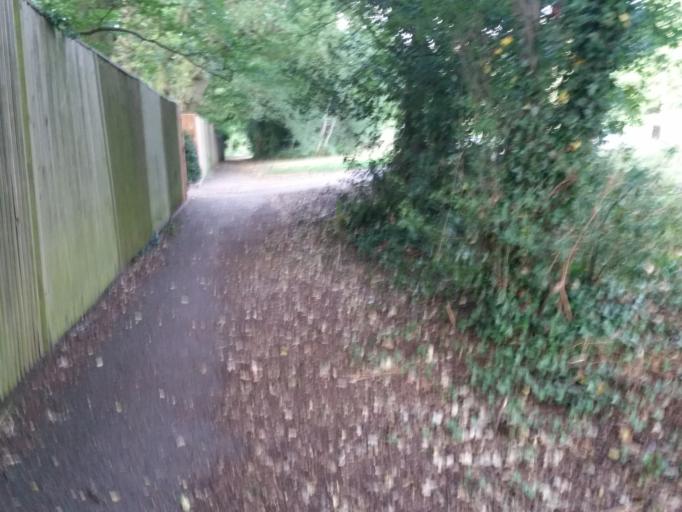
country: GB
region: England
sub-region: Greater London
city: Barnet
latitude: 51.6322
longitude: -0.2206
